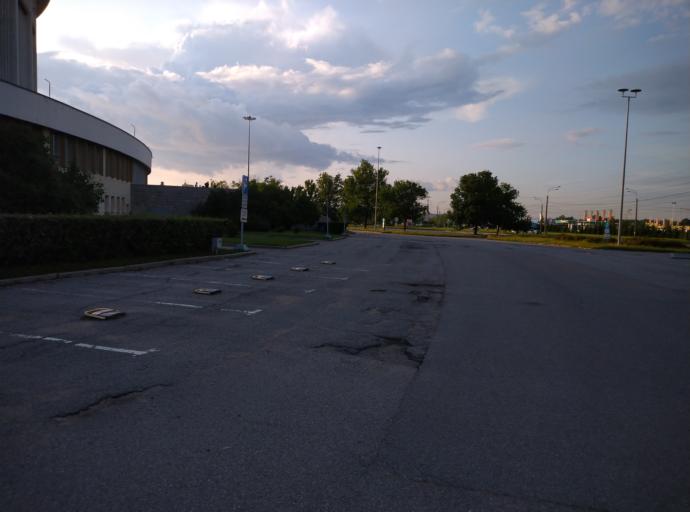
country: RU
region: St.-Petersburg
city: Kupchino
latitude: 59.8689
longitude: 30.3441
